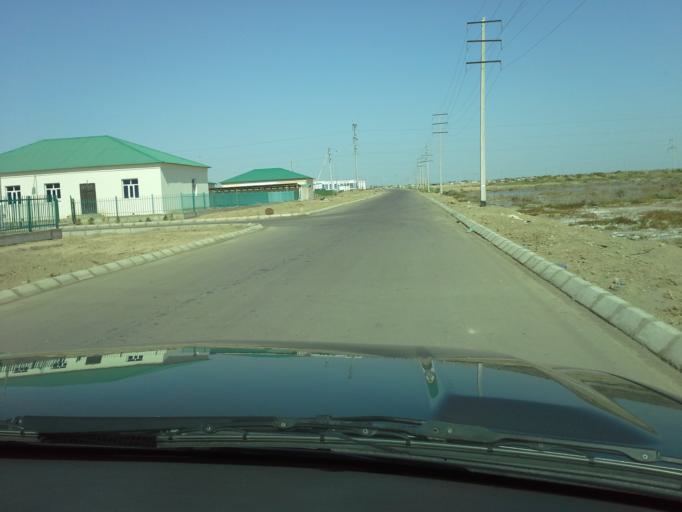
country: TM
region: Dasoguz
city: Dasoguz
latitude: 41.8008
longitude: 59.9460
